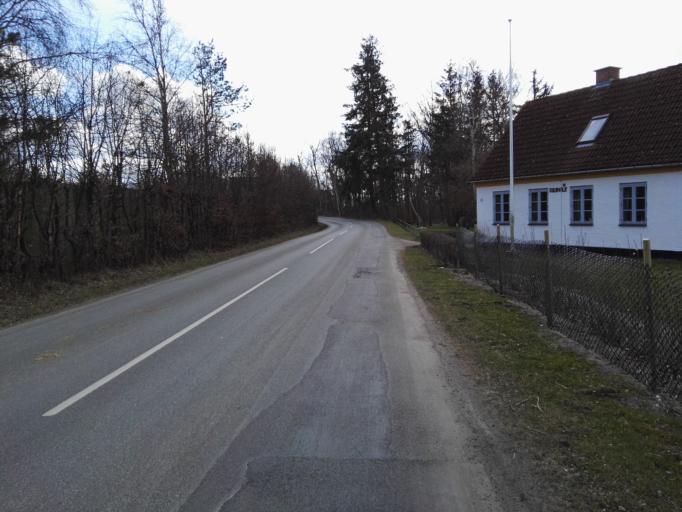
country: DK
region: Zealand
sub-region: Lejre Kommune
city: Ejby
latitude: 55.7630
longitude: 11.8202
